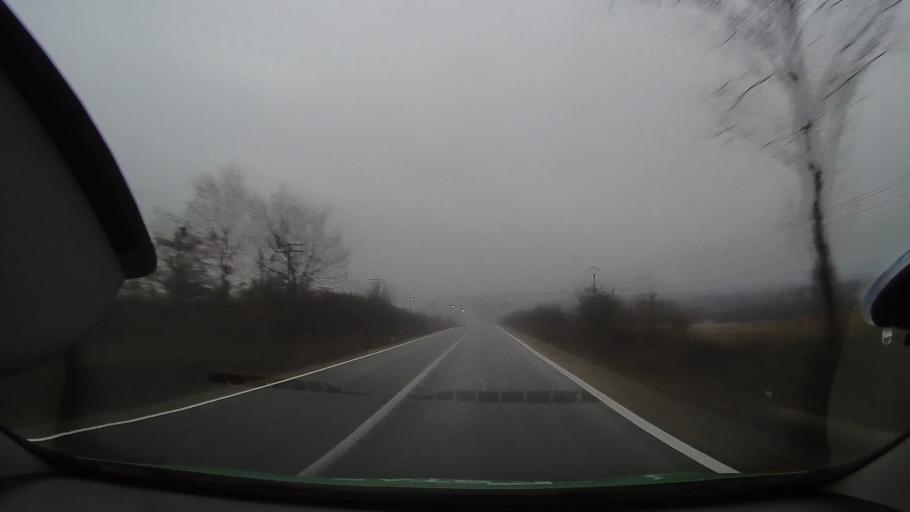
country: RO
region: Bihor
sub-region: Comuna Olcea
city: Olcea
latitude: 46.7156
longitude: 21.9547
